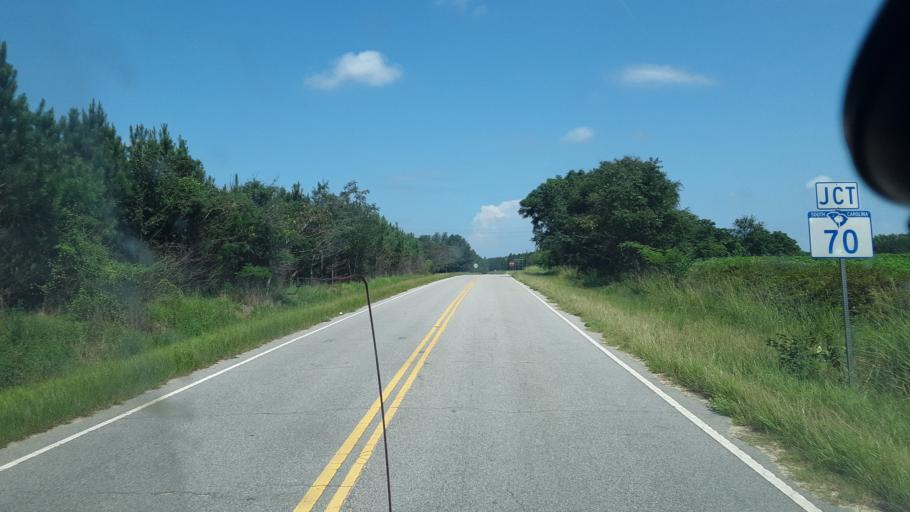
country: US
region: South Carolina
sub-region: Bamberg County
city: Bamberg
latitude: 33.4063
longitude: -81.0161
